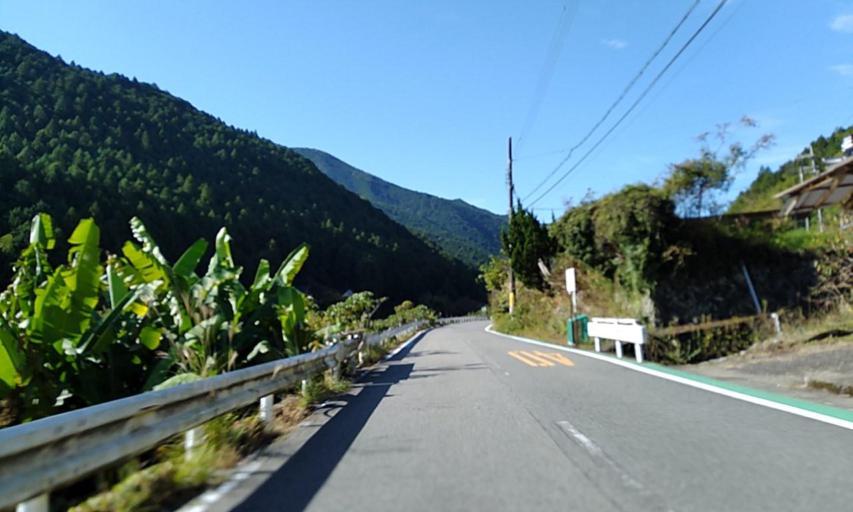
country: JP
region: Wakayama
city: Kainan
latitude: 34.0505
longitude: 135.3532
